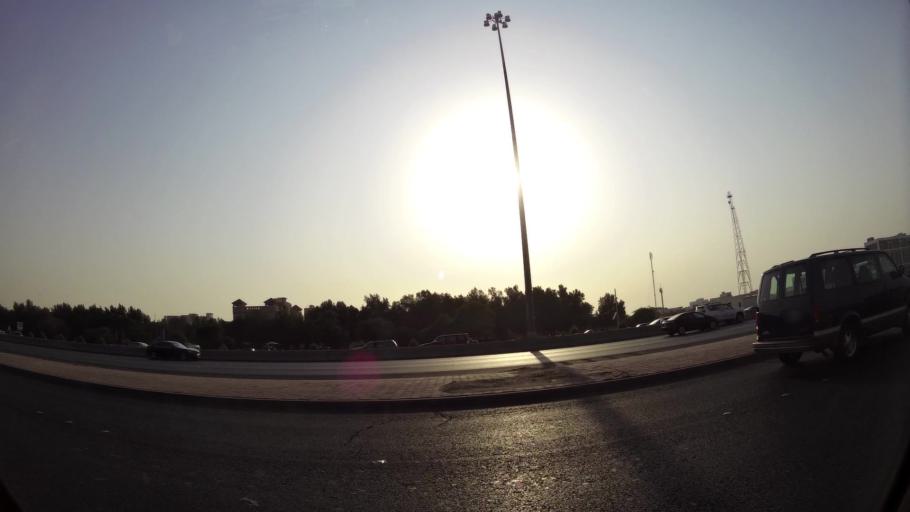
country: KW
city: Bayan
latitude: 29.3091
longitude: 48.0575
